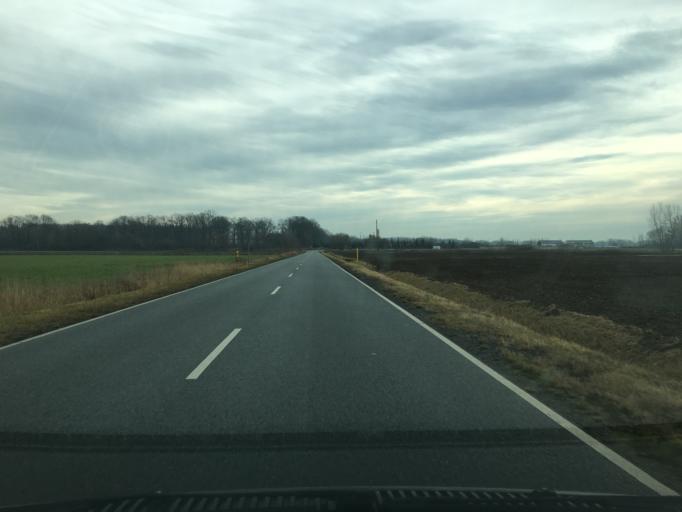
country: PL
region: Lower Silesian Voivodeship
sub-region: Powiat wroclawski
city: Dlugoleka
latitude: 51.1740
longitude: 17.2229
